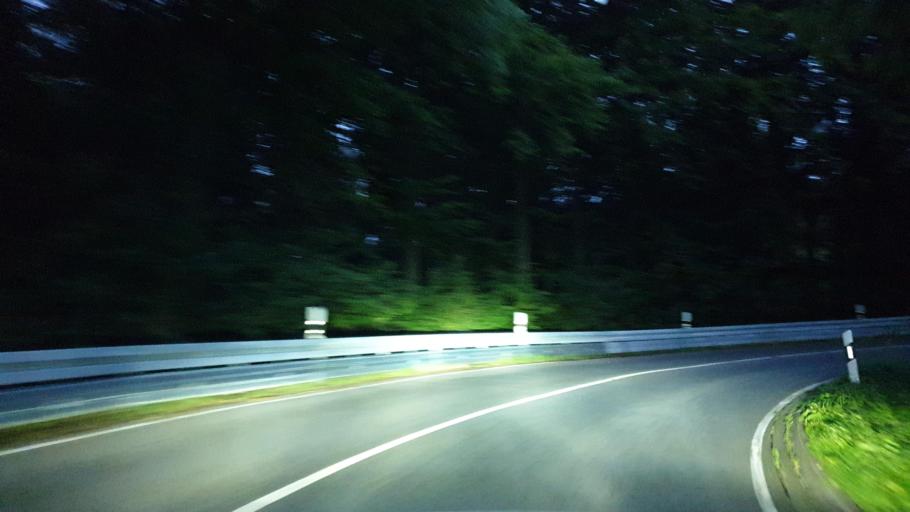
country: DE
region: North Rhine-Westphalia
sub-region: Regierungsbezirk Detmold
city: Huellhorst
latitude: 52.2933
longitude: 8.7129
